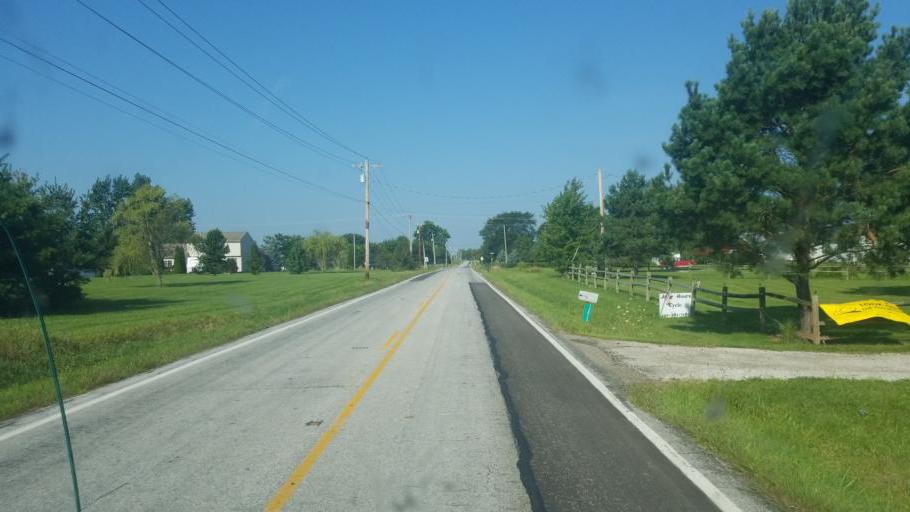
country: US
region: Ohio
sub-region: Lorain County
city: Wellington
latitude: 41.1003
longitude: -82.1591
